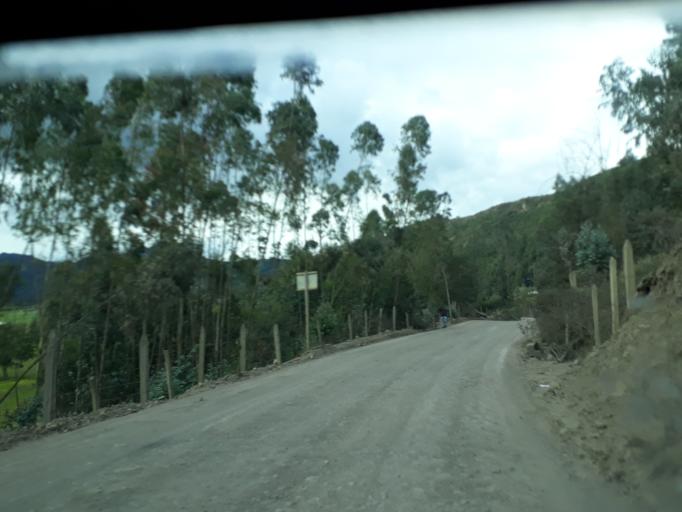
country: CO
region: Cundinamarca
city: Cucunuba
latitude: 5.2471
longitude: -73.7902
